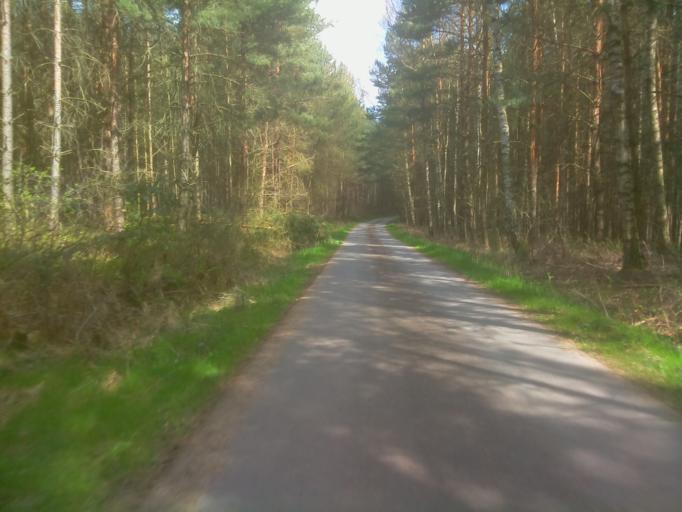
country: DE
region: Thuringia
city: Kleinebersdorf
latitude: 50.7854
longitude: 11.8316
